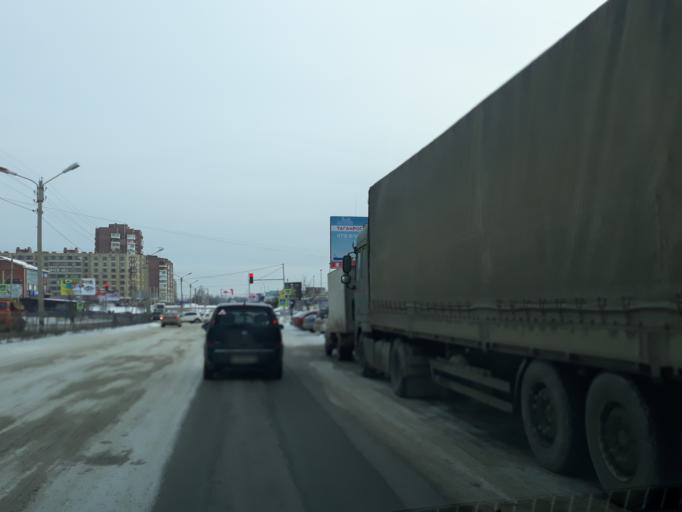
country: RU
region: Rostov
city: Taganrog
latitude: 47.2225
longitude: 38.8594
